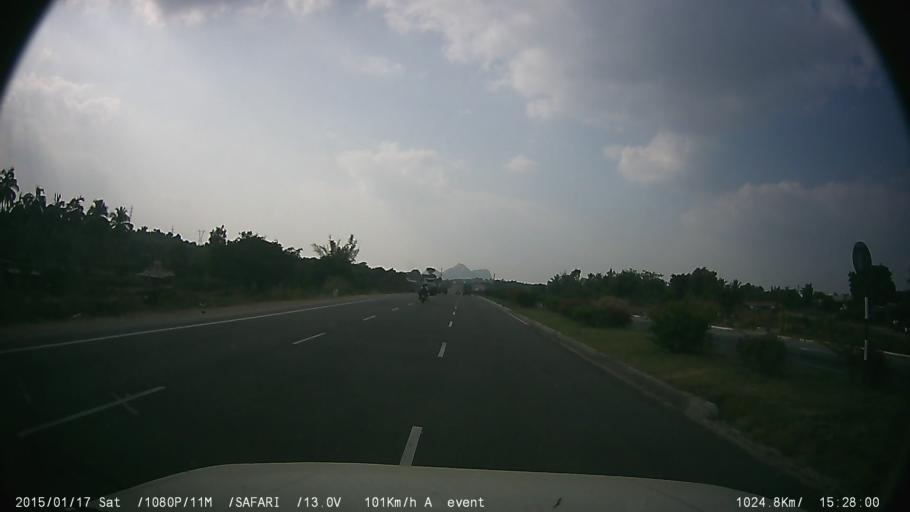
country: IN
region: Tamil Nadu
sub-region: Krishnagiri
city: Krishnagiri
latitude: 12.6406
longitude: 78.0605
